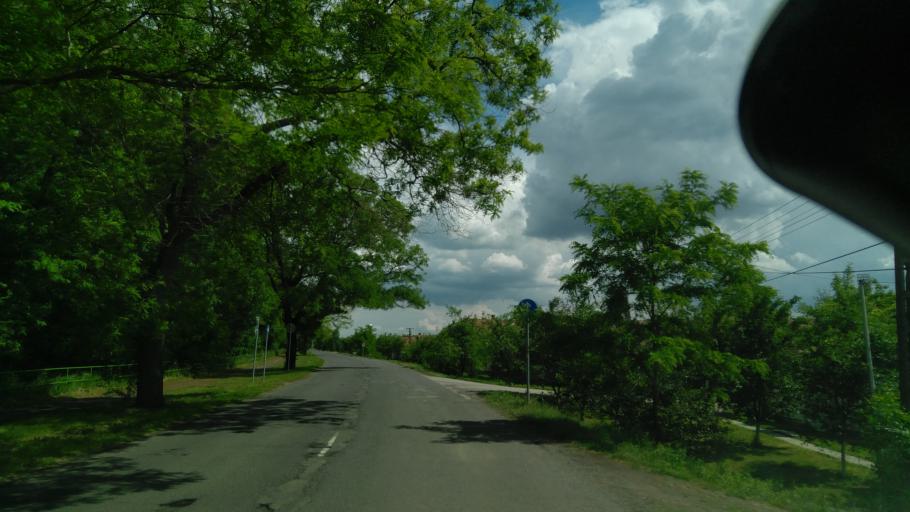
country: HU
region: Bekes
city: Korosladany
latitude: 46.9721
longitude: 21.0627
